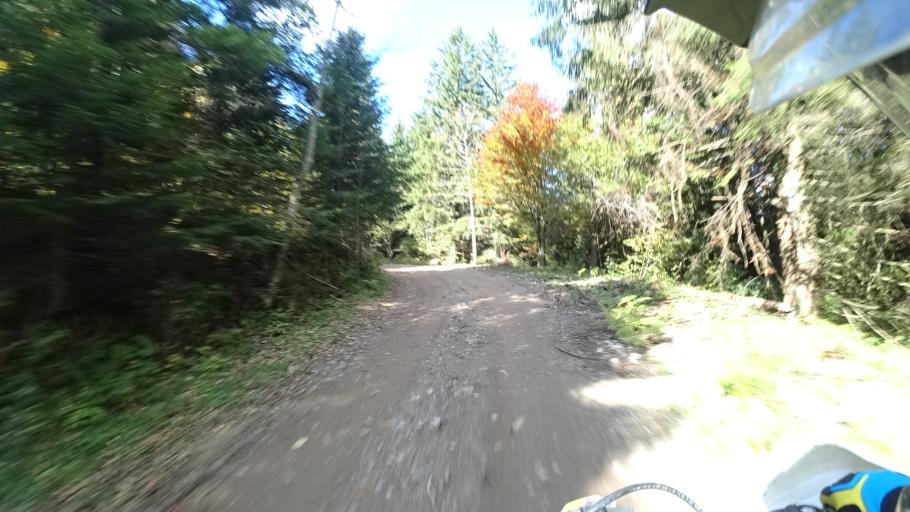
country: HR
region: Karlovacka
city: Plaski
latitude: 45.0670
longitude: 15.3428
